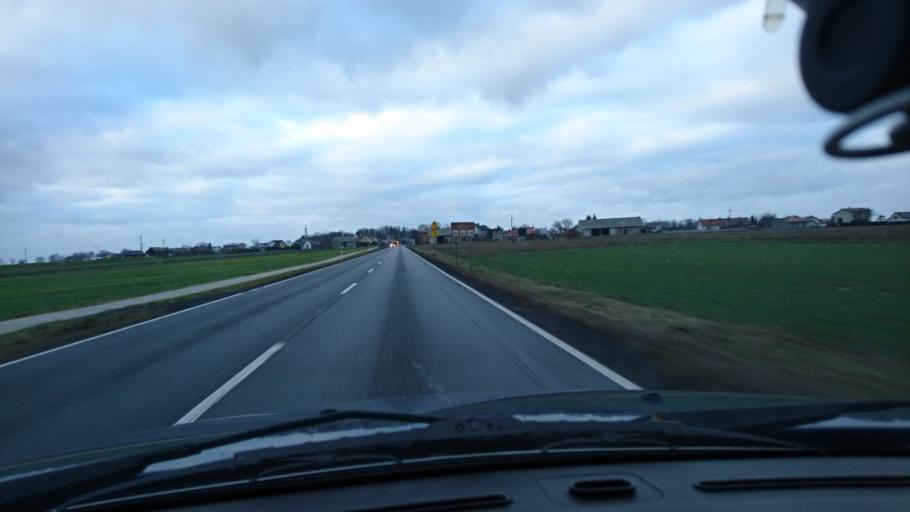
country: PL
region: Greater Poland Voivodeship
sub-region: Powiat kepinski
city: Opatow
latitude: 51.1733
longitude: 18.1455
